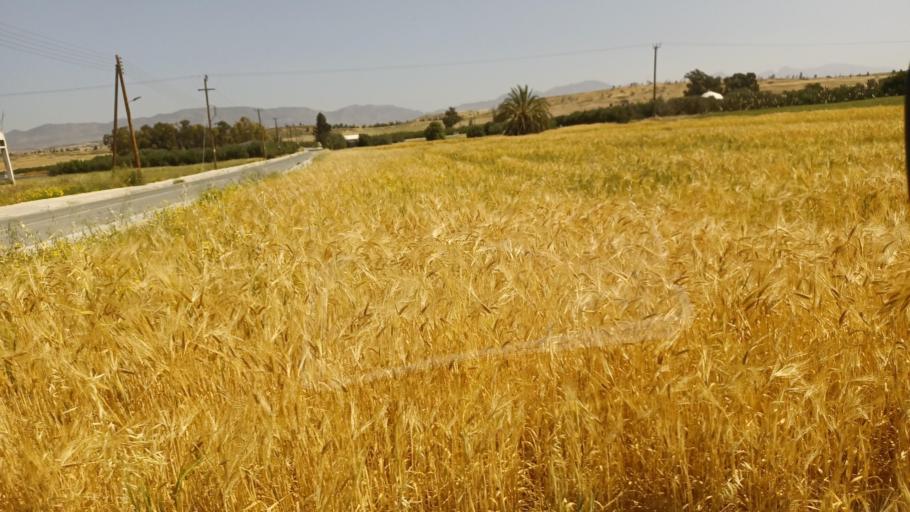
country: CY
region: Lefkosia
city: Mammari
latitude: 35.1816
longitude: 33.2092
